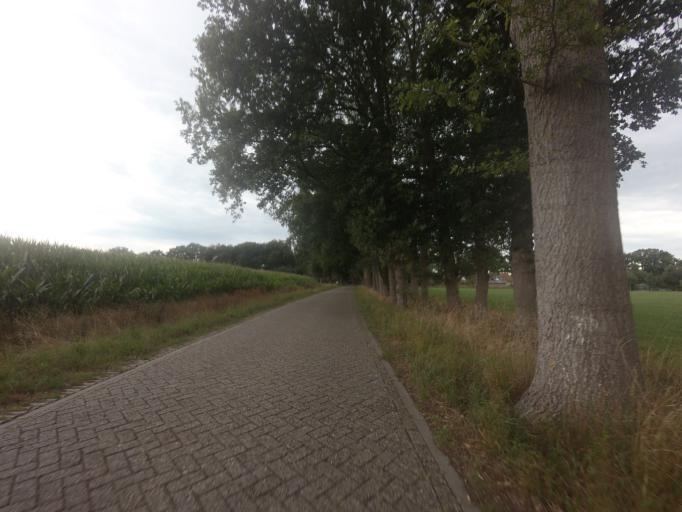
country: NL
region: Overijssel
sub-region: Gemeente Raalte
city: Raalte
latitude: 52.3372
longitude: 6.2964
